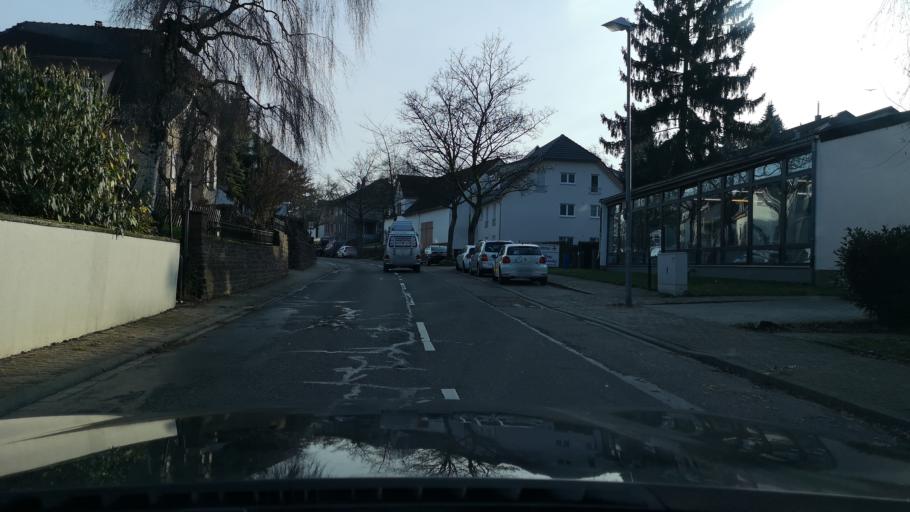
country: DE
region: Baden-Wuerttemberg
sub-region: Karlsruhe Region
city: Ettlingen
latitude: 48.9708
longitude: 8.4762
